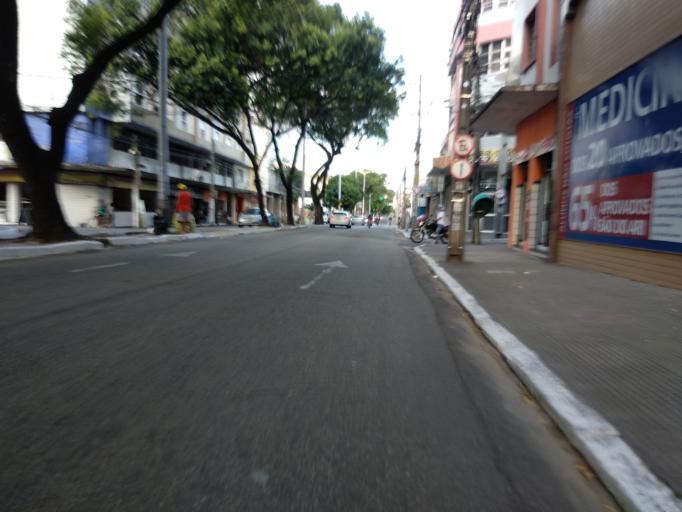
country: BR
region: Ceara
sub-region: Fortaleza
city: Fortaleza
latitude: -3.7320
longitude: -38.5292
